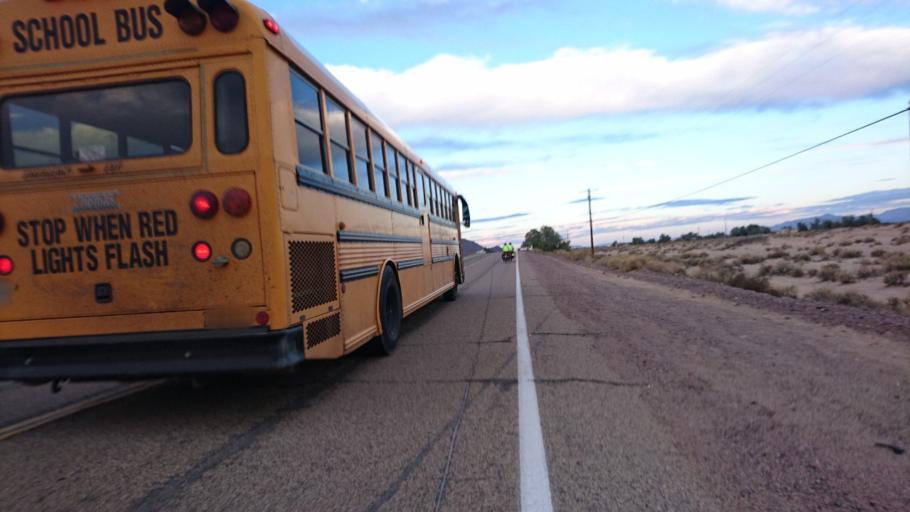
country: US
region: California
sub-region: San Bernardino County
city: Barstow
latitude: 34.8161
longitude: -116.6246
